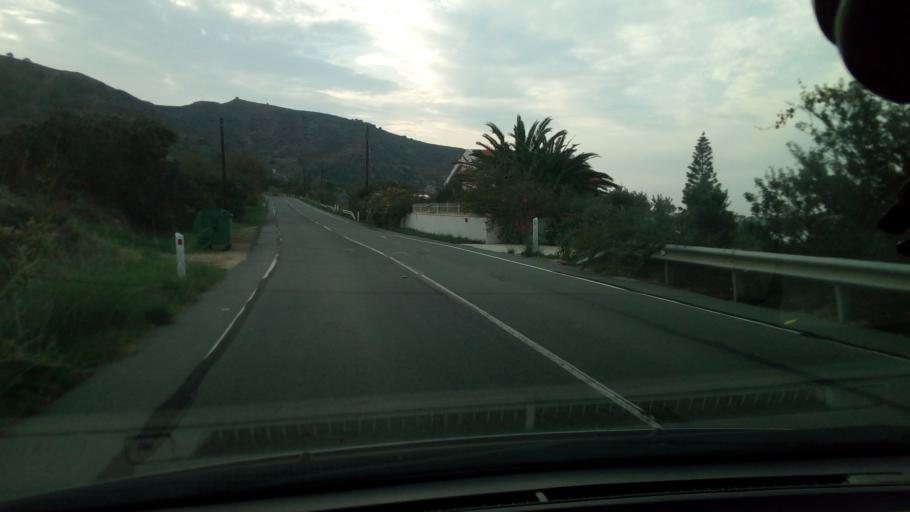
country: CY
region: Lefkosia
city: Kato Pyrgos
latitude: 35.1694
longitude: 32.5690
